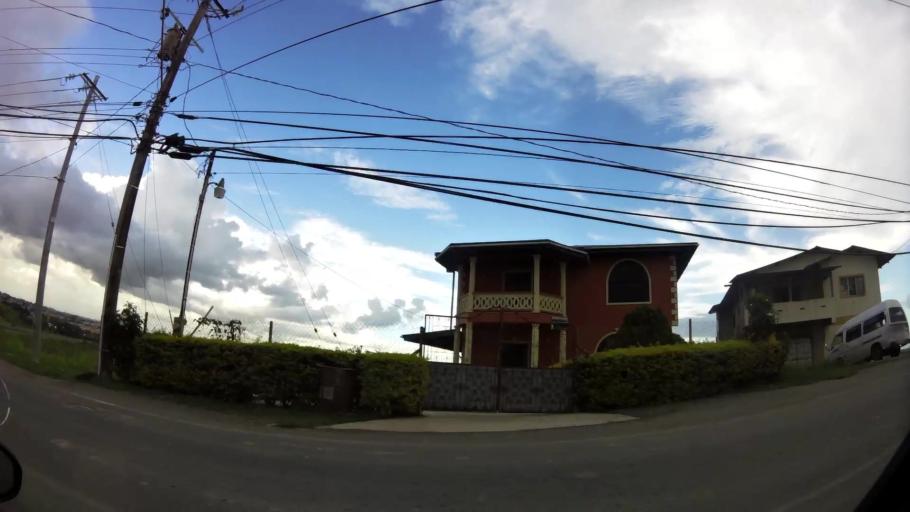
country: TT
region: City of San Fernando
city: Mon Repos
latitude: 10.2447
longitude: -61.4435
